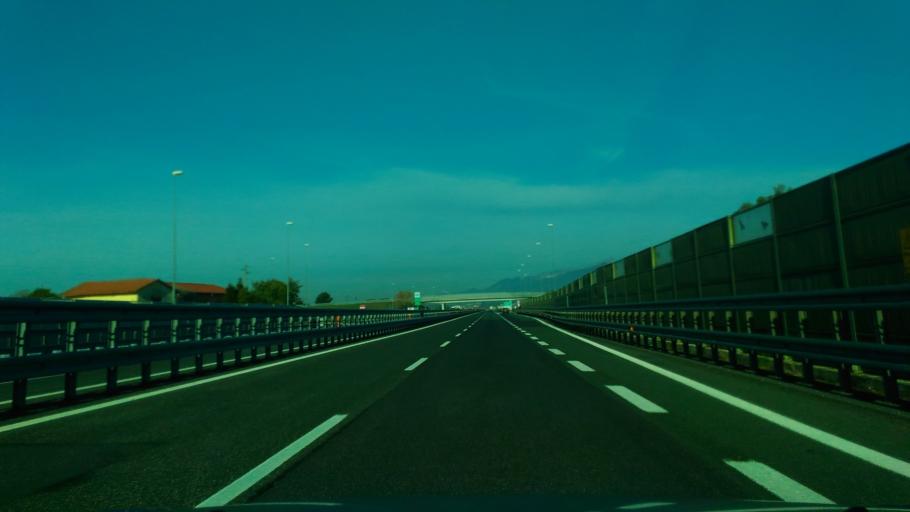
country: IT
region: Tuscany
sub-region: Provincia di Lucca
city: Viareggio
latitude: 43.8852
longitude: 10.2648
